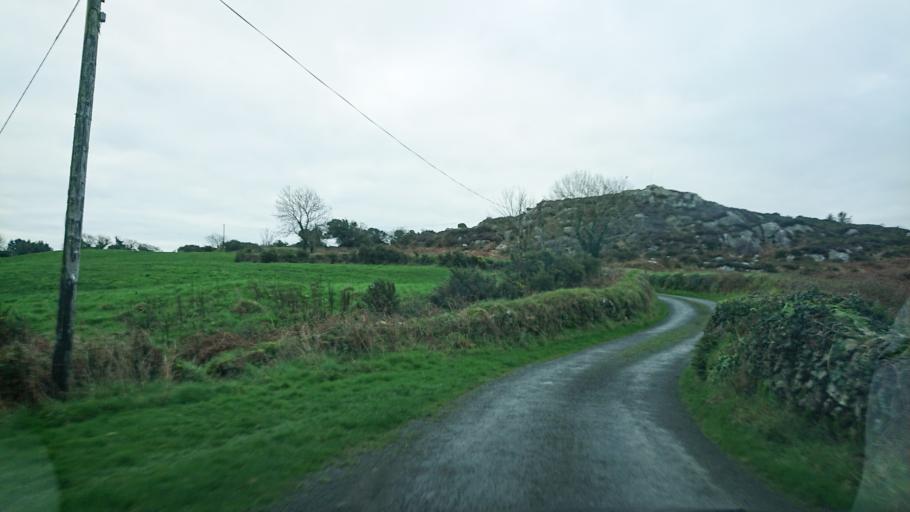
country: IE
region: Leinster
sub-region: Kilkenny
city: Mooncoin
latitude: 52.2109
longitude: -7.2690
